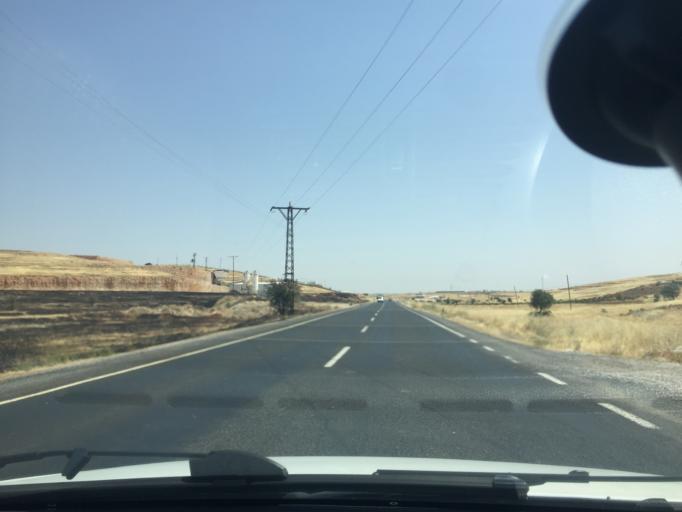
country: TR
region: Mardin
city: Kindirip
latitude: 37.4596
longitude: 41.2374
